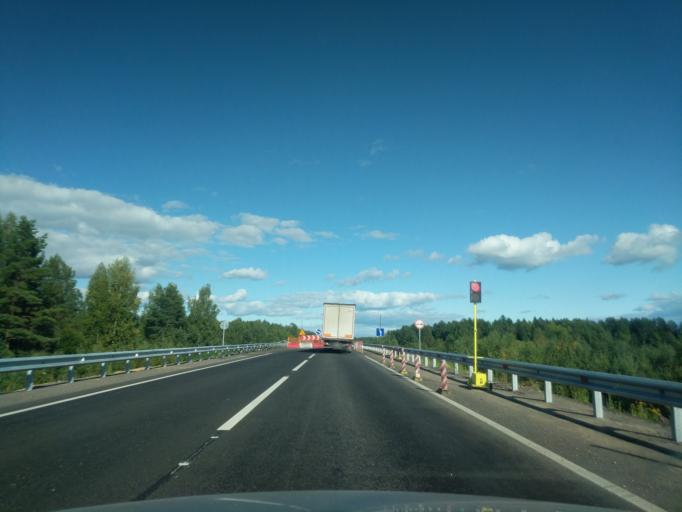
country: RU
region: Kostroma
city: Makar'yev
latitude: 57.8483
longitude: 43.6800
